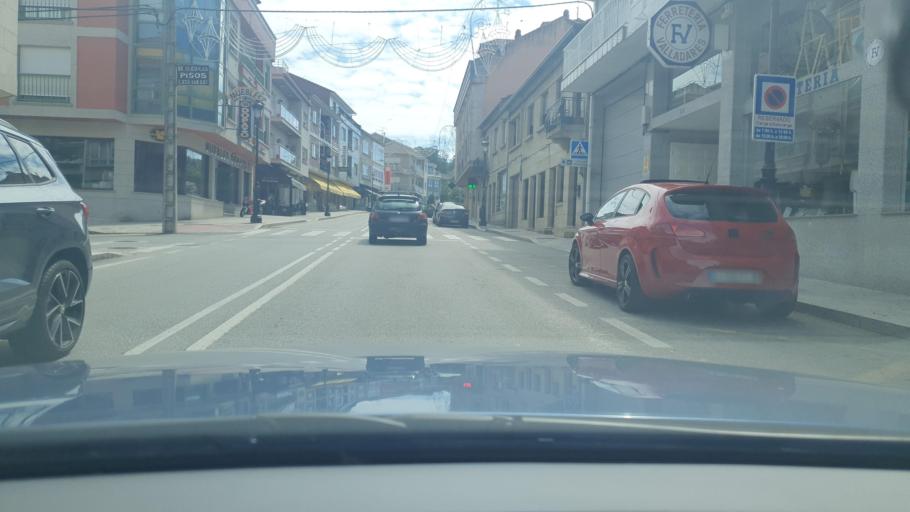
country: ES
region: Galicia
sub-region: Provincia de Pontevedra
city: Sanxenxo
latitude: 42.4417
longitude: -8.8372
